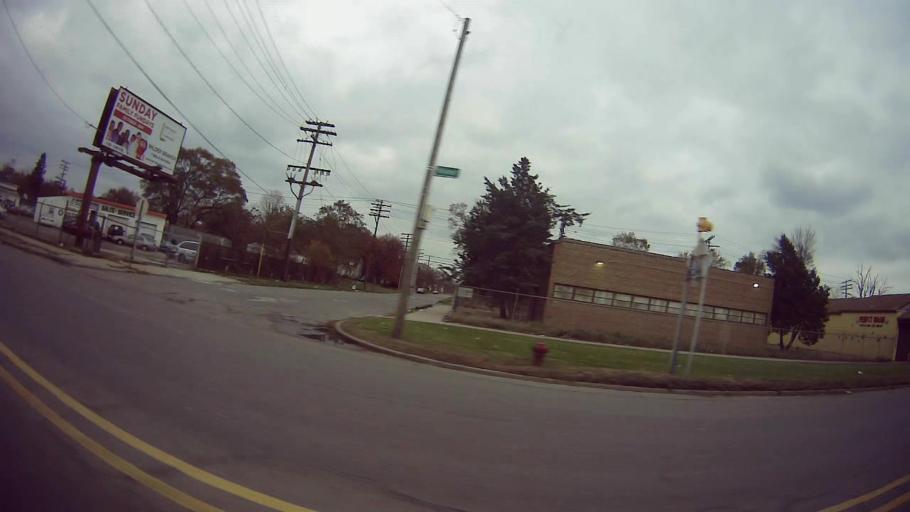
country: US
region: Michigan
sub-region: Macomb County
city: Warren
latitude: 42.4433
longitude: -83.0050
